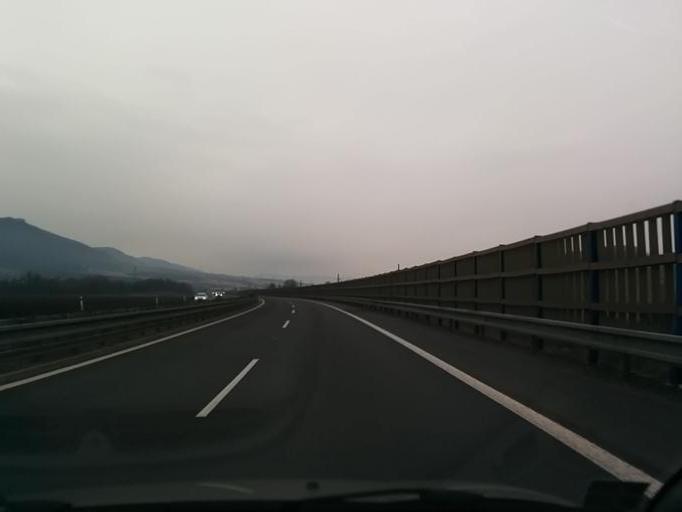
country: SK
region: Banskobystricky
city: Zarnovica
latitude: 48.5215
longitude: 18.7371
